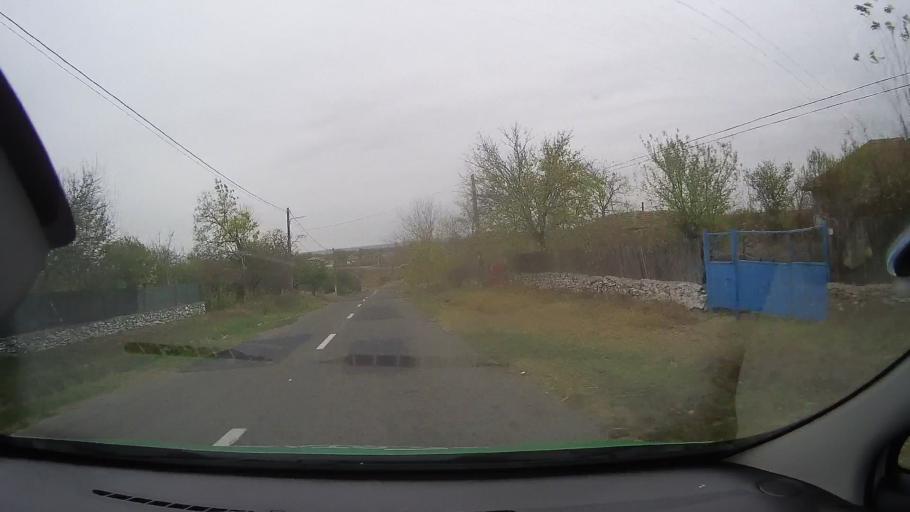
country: RO
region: Constanta
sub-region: Comuna Vulturu
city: Vulturu
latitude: 44.6987
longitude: 28.2408
